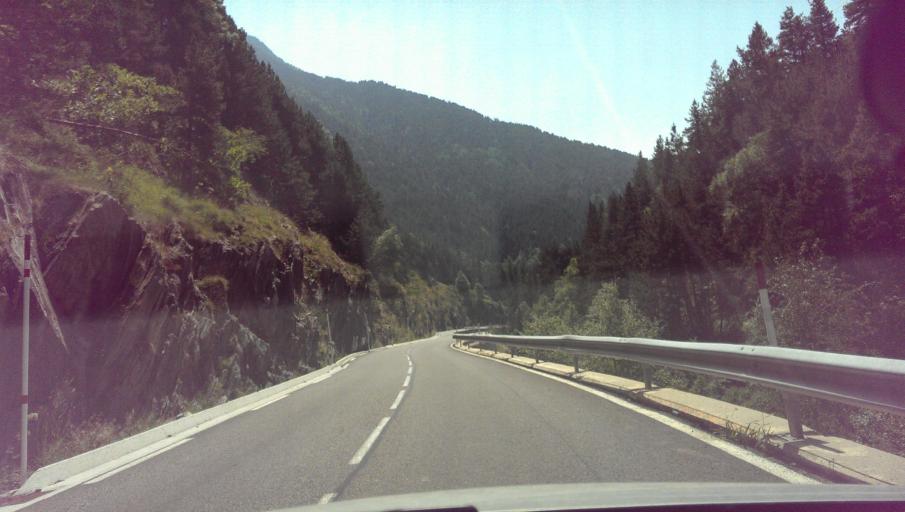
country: AD
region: Encamp
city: Pas de la Casa
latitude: 42.5432
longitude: 1.8267
